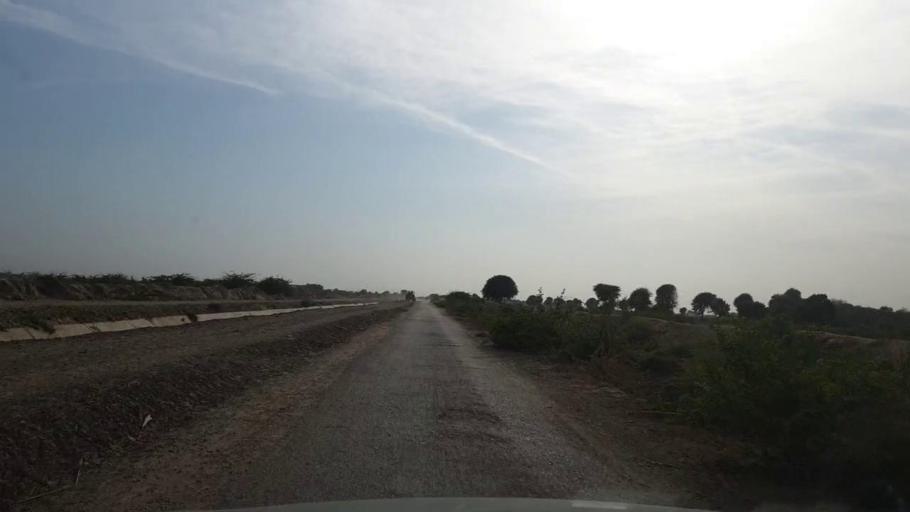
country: PK
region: Sindh
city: Kunri
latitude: 25.1583
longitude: 69.5146
